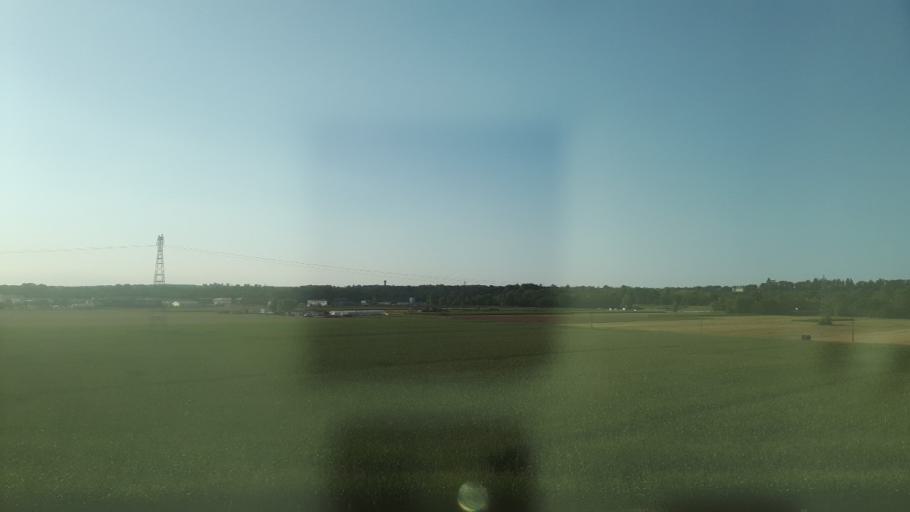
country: FR
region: Centre
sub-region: Departement d'Indre-et-Loire
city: Vouvray
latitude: 47.3946
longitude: 0.7975
